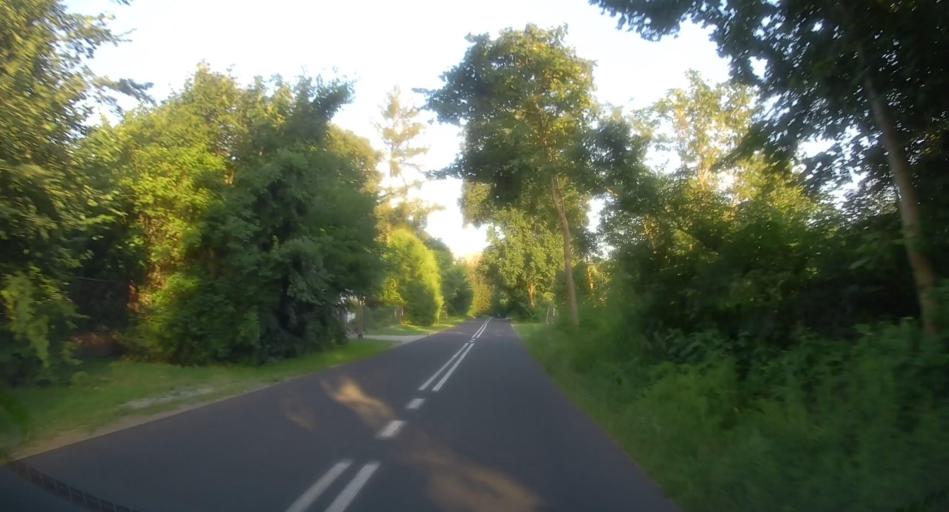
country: PL
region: Lodz Voivodeship
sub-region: Powiat skierniewicki
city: Kowiesy
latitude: 51.8978
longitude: 20.3753
